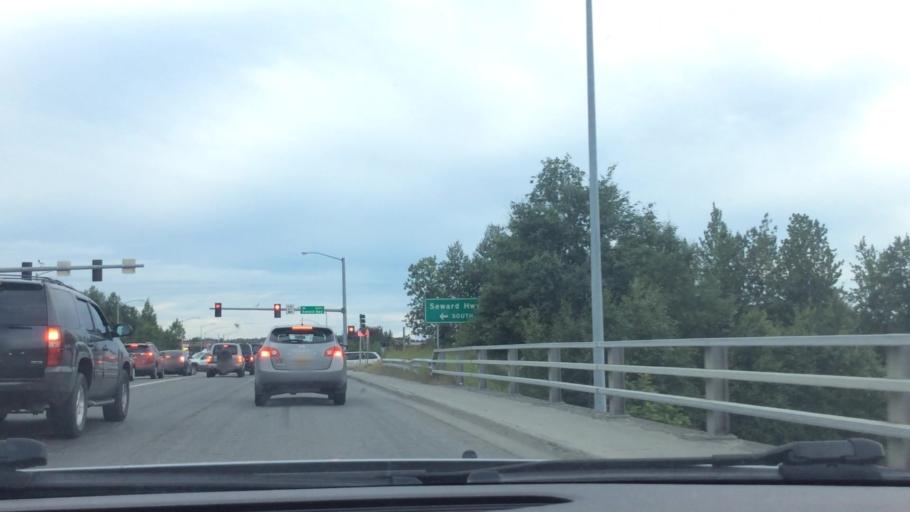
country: US
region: Alaska
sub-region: Anchorage Municipality
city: Anchorage
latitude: 61.1809
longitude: -149.8606
